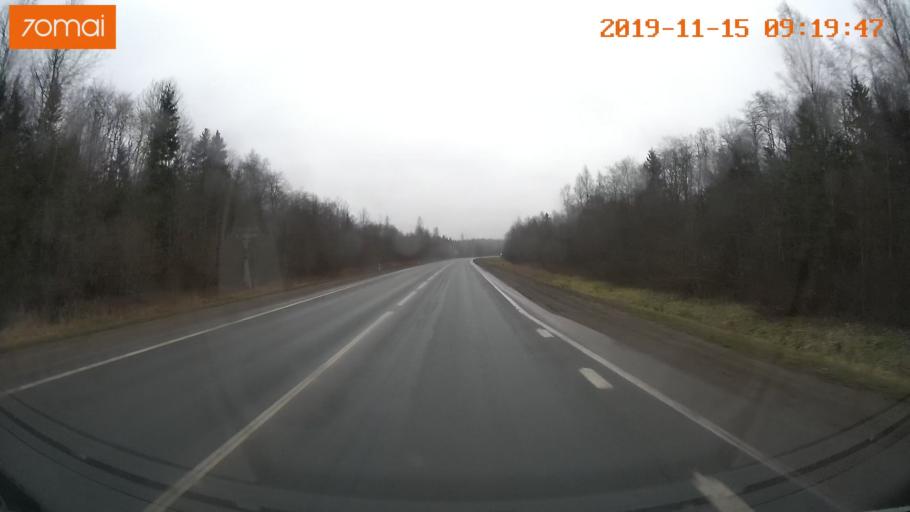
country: RU
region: Vologda
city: Tonshalovo
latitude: 59.2866
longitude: 38.0226
